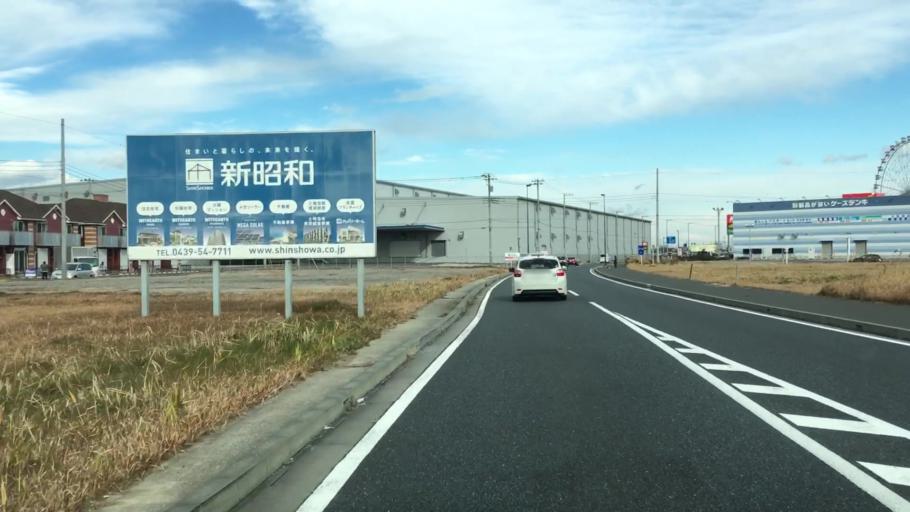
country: JP
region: Chiba
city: Kisarazu
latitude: 35.4379
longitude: 139.9274
